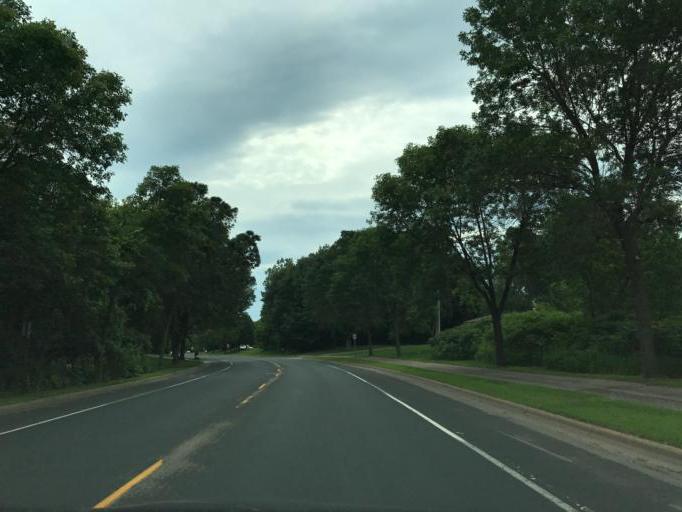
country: US
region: Minnesota
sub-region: Hennepin County
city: Osseo
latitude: 45.0839
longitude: -93.4074
